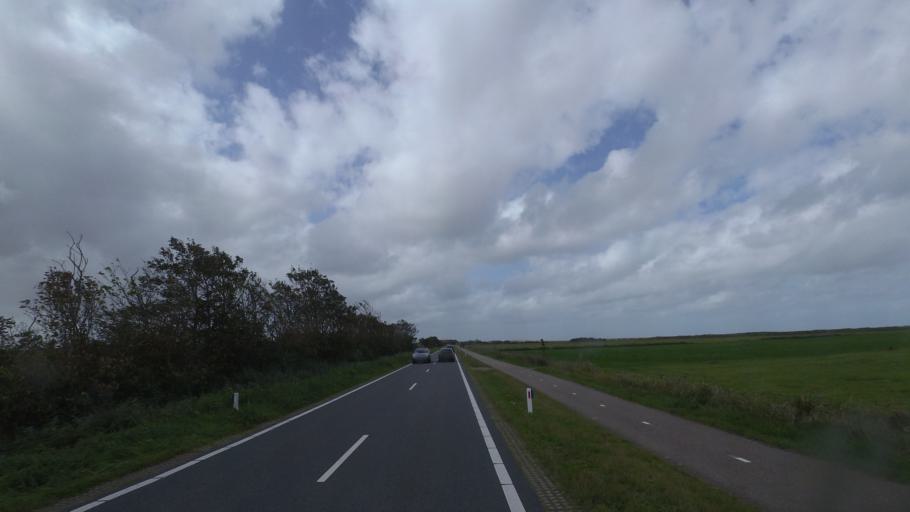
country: NL
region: Friesland
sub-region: Gemeente Ameland
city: Hollum
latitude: 53.4459
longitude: 5.6786
